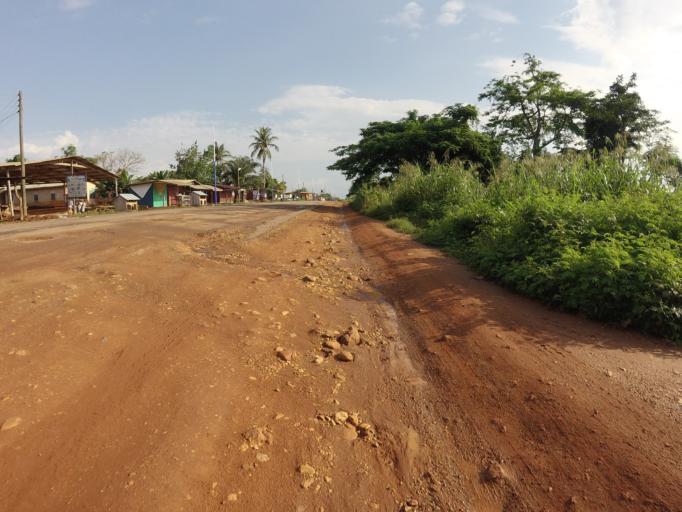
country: GH
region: Volta
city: Hohoe
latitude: 7.1161
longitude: 0.4566
